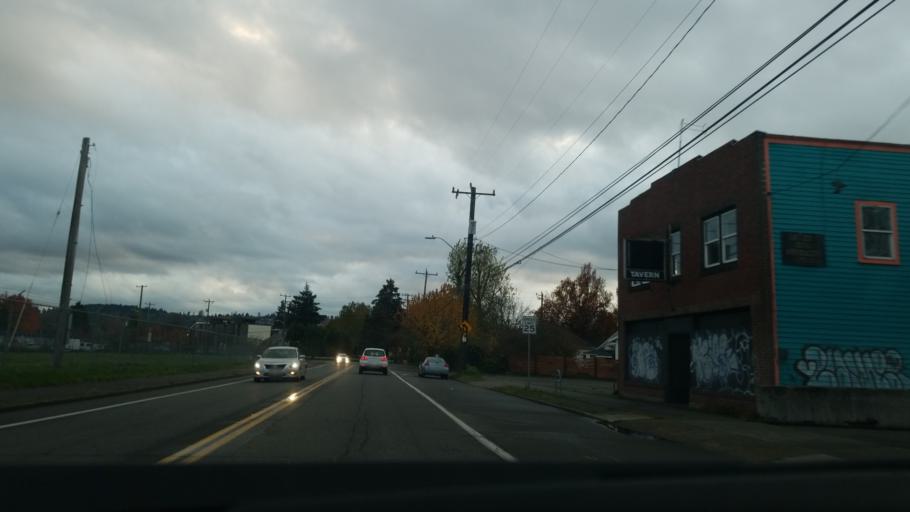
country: US
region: Washington
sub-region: King County
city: White Center
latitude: 47.5460
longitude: -122.3169
